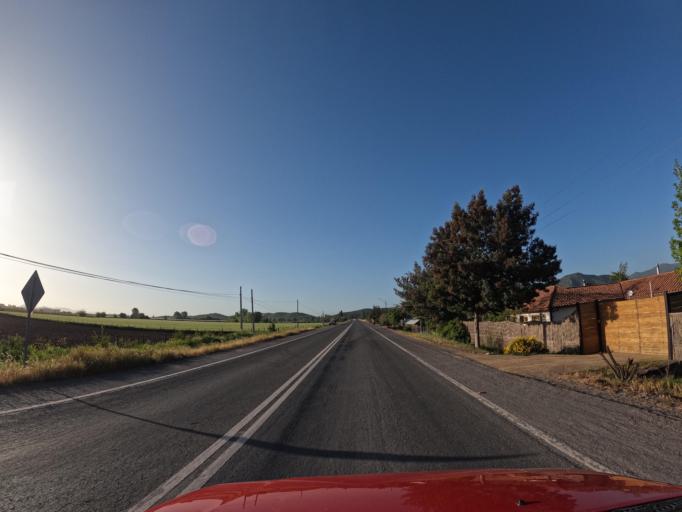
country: CL
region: O'Higgins
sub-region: Provincia de Colchagua
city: Santa Cruz
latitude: -34.4435
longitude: -71.3671
